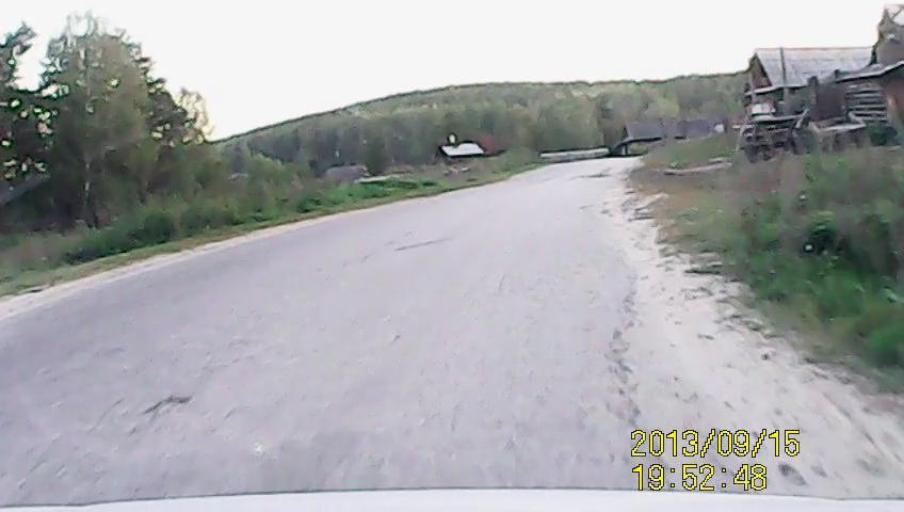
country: RU
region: Chelyabinsk
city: Kyshtym
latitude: 55.7667
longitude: 60.4867
